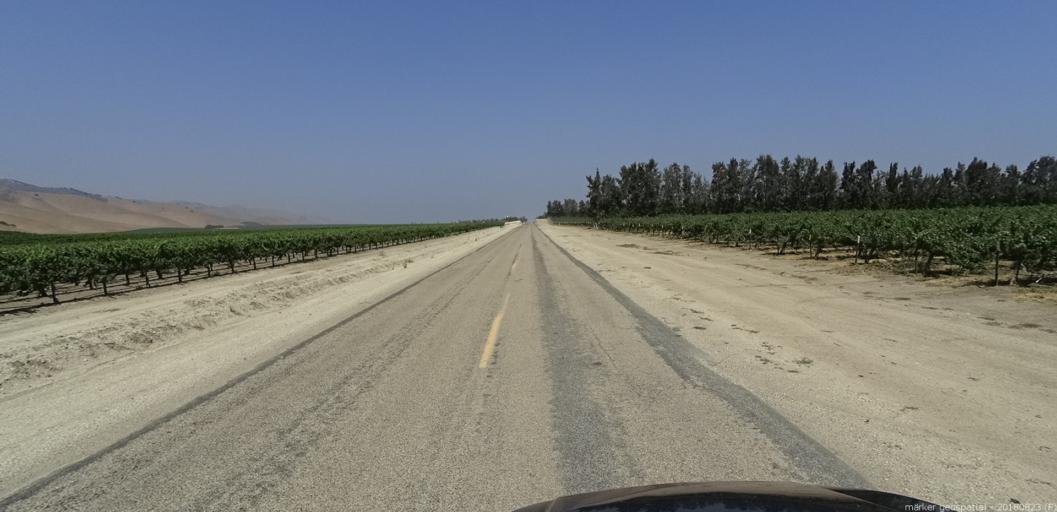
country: US
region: California
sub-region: Monterey County
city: King City
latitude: 36.2423
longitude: -121.1871
